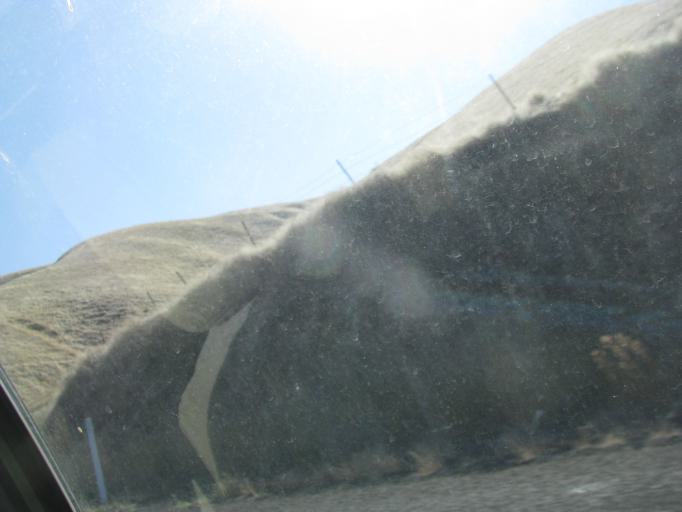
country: US
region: Washington
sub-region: Asotin County
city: Asotin
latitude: 46.3194
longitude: -117.0524
